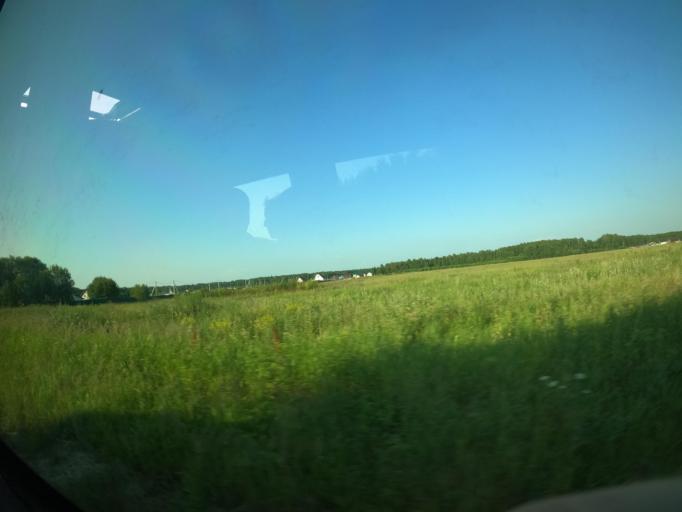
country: RU
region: Moskovskaya
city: Obolensk
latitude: 54.9390
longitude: 37.2443
